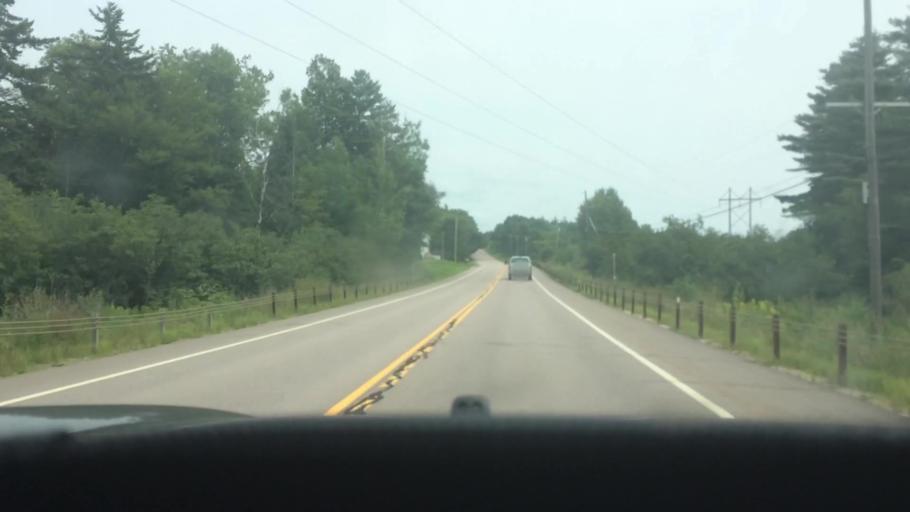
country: US
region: New York
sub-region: Franklin County
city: Malone
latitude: 44.8528
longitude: -74.0787
